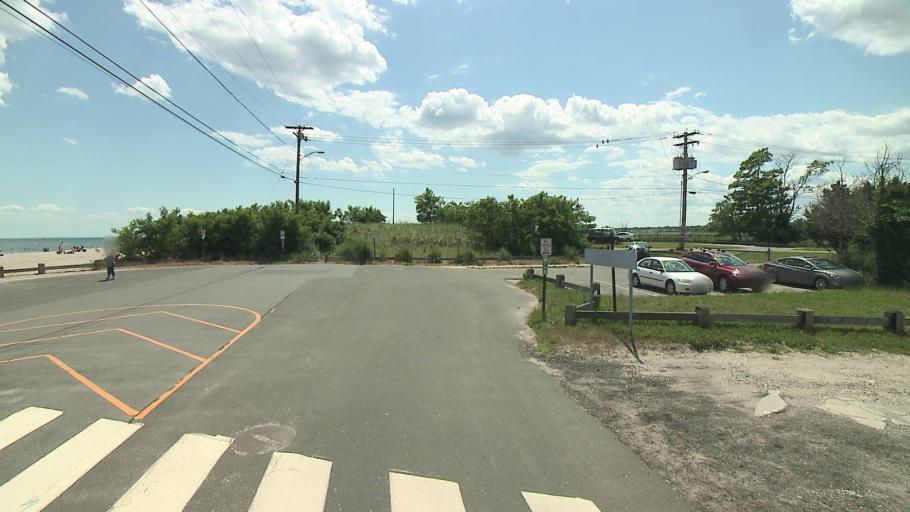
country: US
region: Connecticut
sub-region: New Haven County
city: Milford
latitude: 41.2006
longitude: -73.0651
